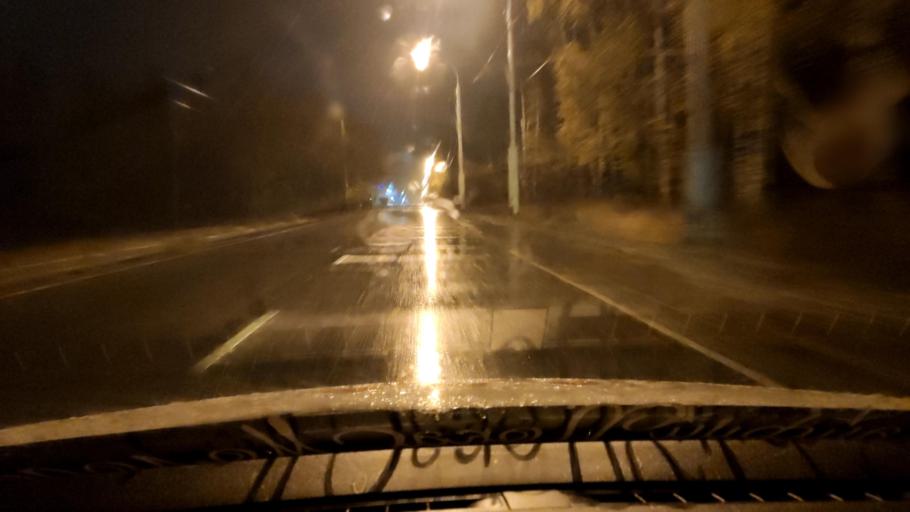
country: RU
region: Voronezj
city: Somovo
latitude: 51.7167
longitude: 39.2939
